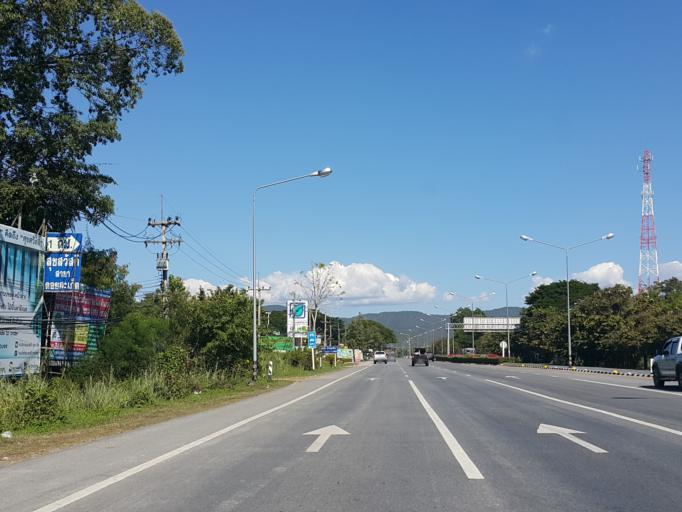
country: TH
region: Chiang Mai
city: San Sai
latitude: 18.8719
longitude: 99.1323
